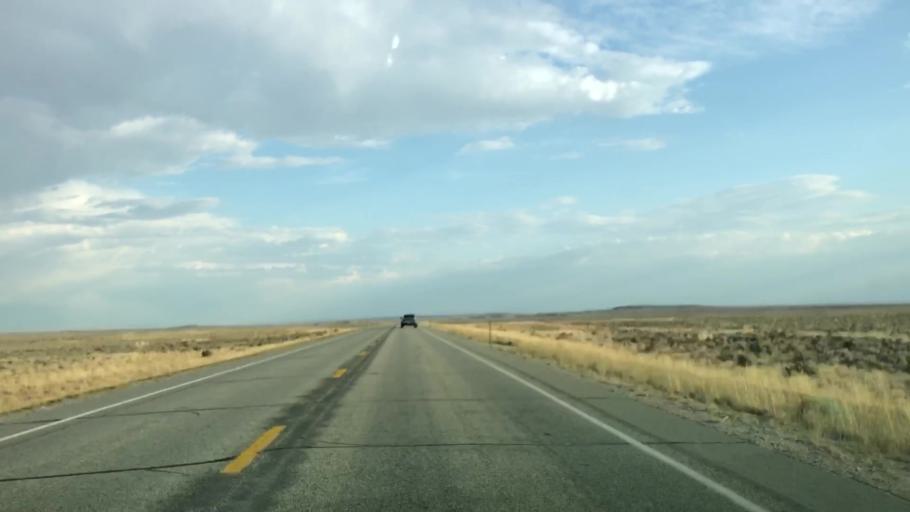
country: US
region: Wyoming
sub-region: Sublette County
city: Pinedale
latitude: 42.3902
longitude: -109.5401
